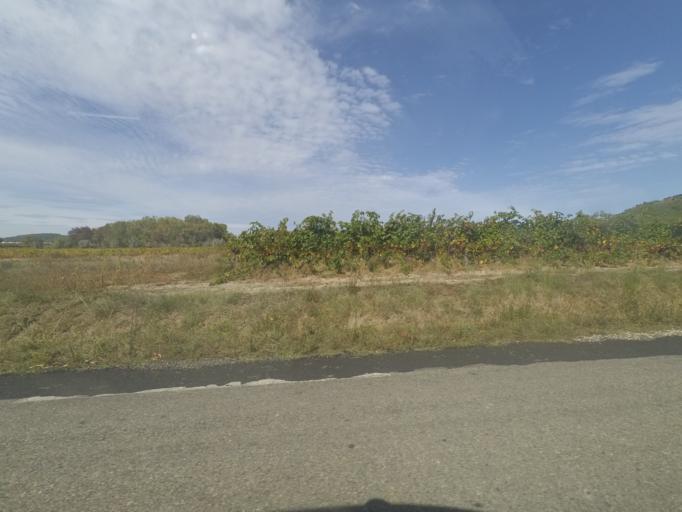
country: FR
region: Languedoc-Roussillon
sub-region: Departement du Gard
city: Nages-et-Solorgues
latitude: 43.7869
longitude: 4.2167
